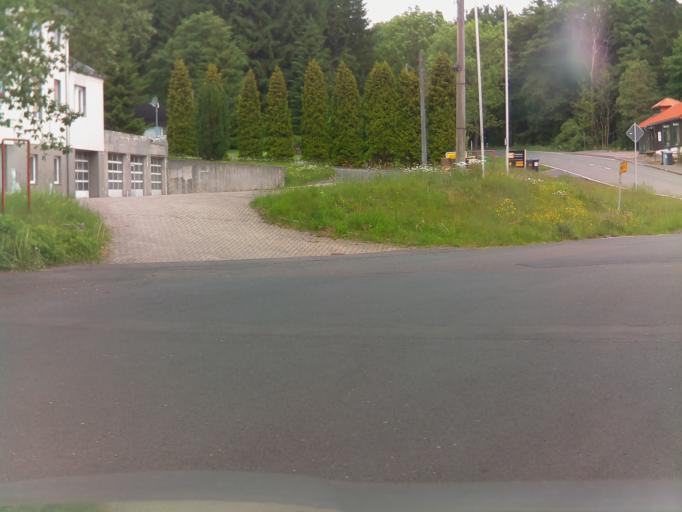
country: DE
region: Thuringia
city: Schmiedefeld am Rennsteig
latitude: 50.6077
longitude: 10.8047
